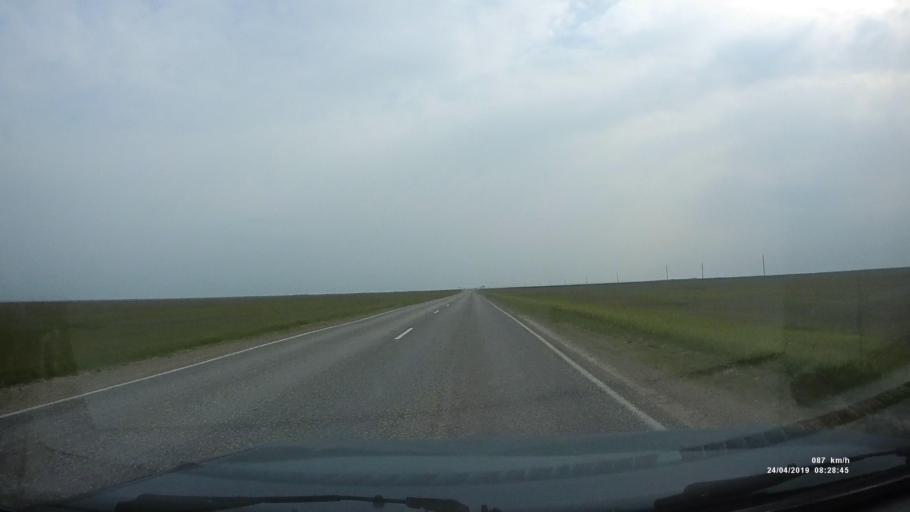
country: RU
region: Kalmykiya
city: Priyutnoye
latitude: 46.1468
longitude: 43.8203
